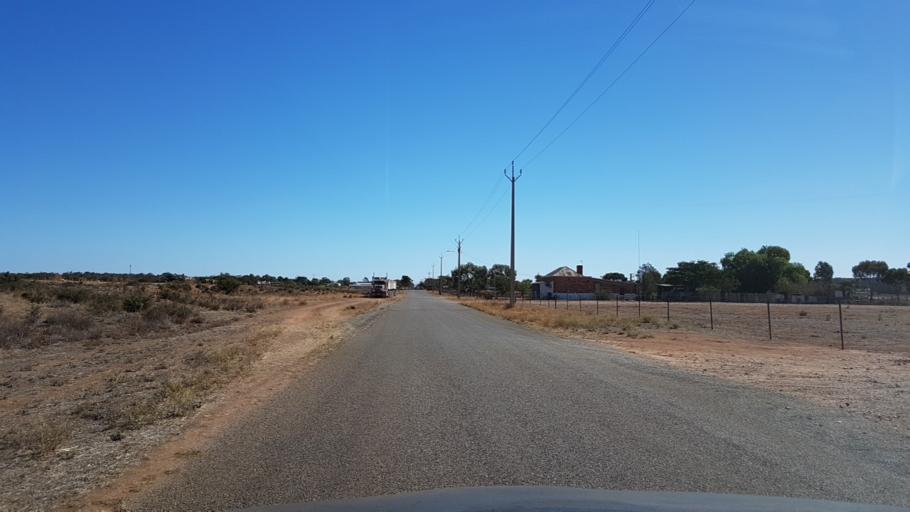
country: AU
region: South Australia
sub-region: Peterborough
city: Peterborough
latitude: -32.9719
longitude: 138.8532
